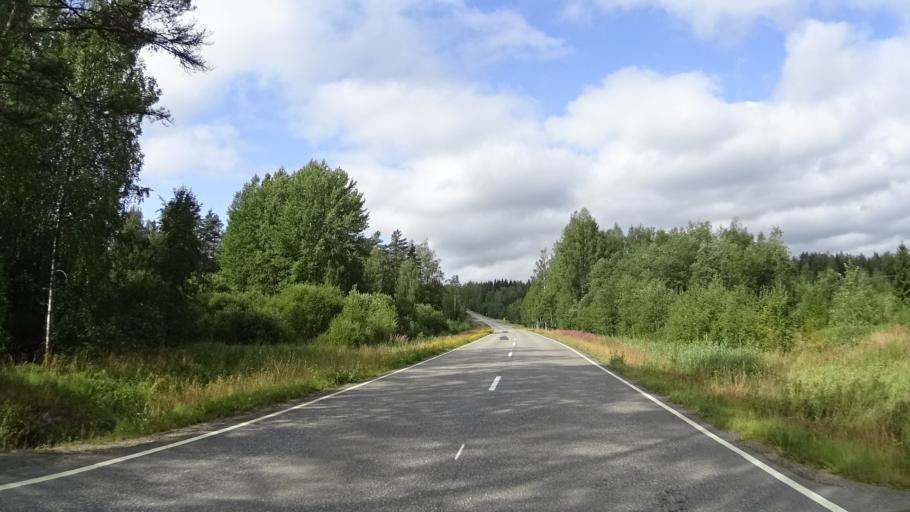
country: FI
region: Pirkanmaa
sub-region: Tampere
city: Luopioinen
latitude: 61.4959
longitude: 24.7919
